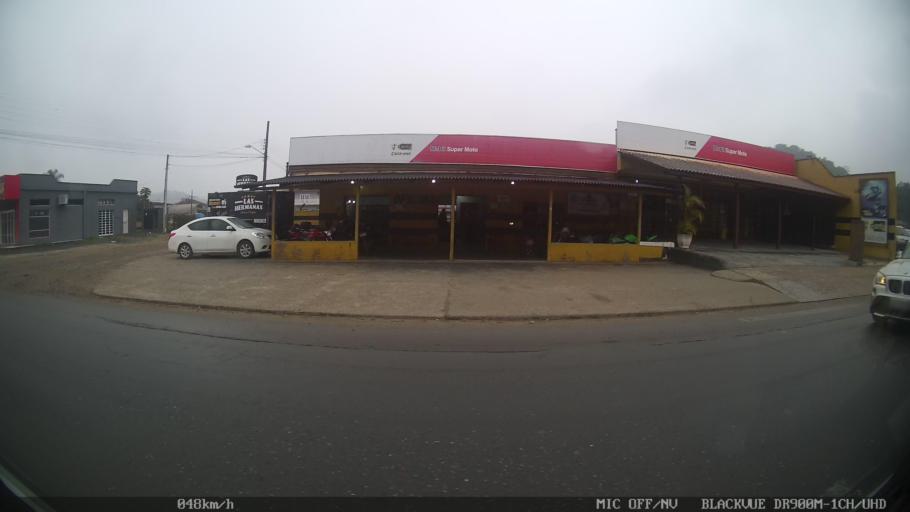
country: BR
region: Santa Catarina
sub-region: Joinville
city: Joinville
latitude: -26.2163
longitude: -48.8202
